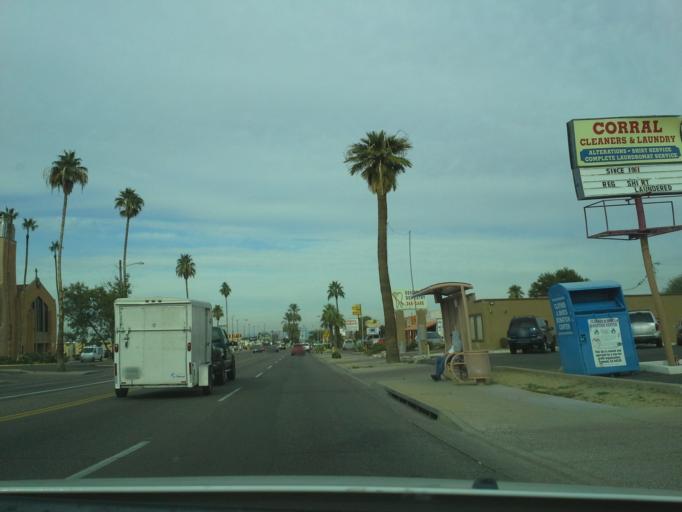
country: US
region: Arizona
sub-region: Maricopa County
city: Phoenix
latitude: 33.3887
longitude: -112.0732
